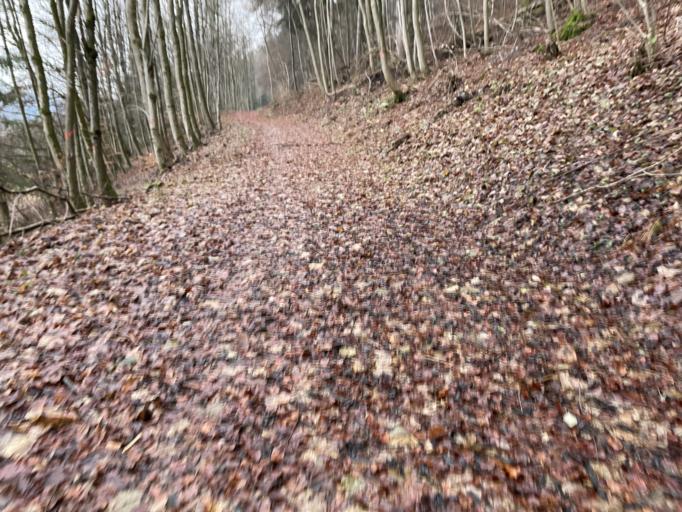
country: CH
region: Bern
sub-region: Bern-Mittelland District
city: Munsingen
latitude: 46.8729
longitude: 7.5353
